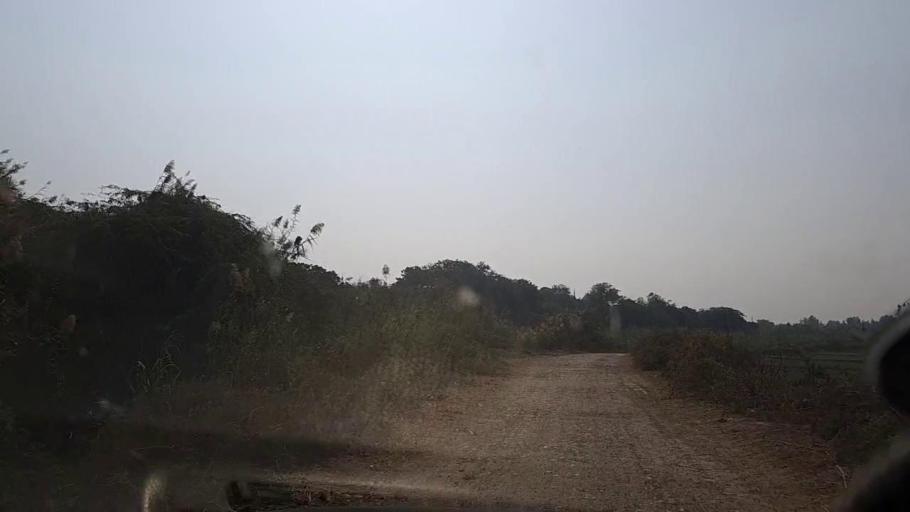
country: PK
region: Sindh
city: Thatta
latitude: 24.6535
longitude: 67.9104
